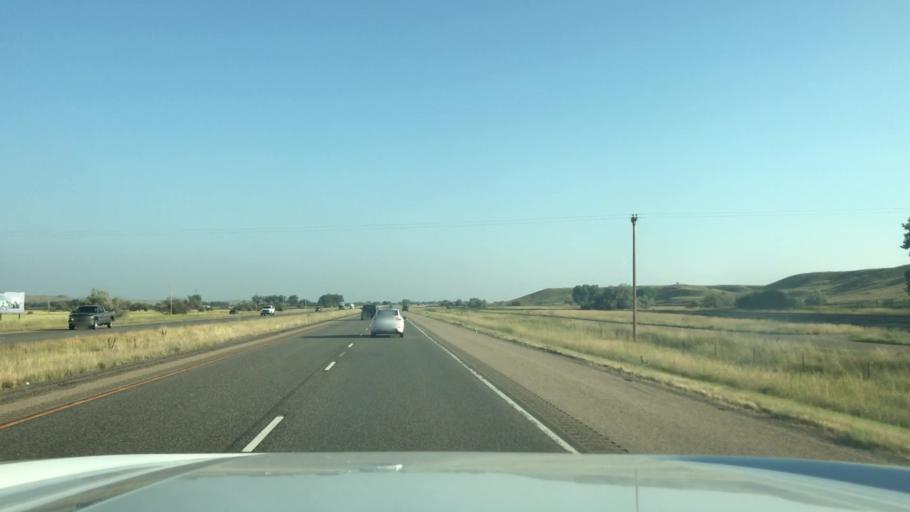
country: US
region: Montana
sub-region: Big Horn County
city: Crow Agency
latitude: 45.6374
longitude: -107.4705
